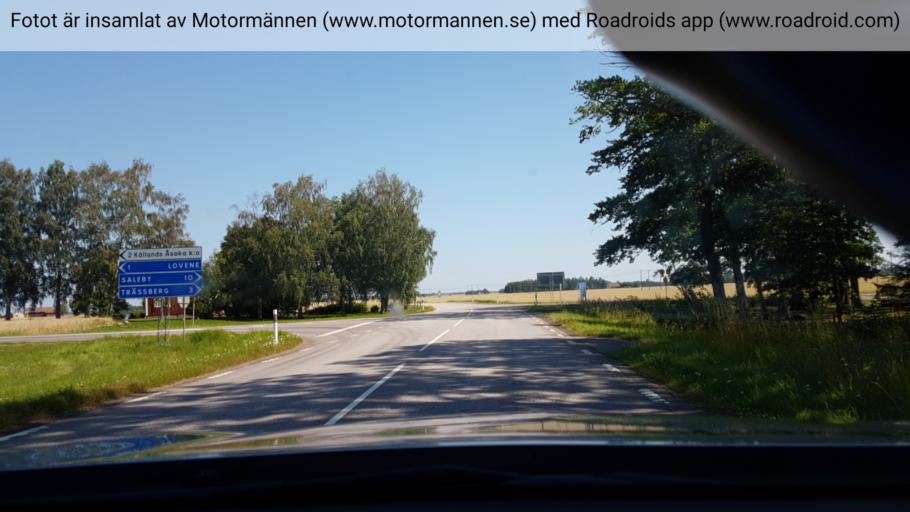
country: SE
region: Vaestra Goetaland
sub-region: Lidkopings Kommun
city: Lidkoping
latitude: 58.4366
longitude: 13.0564
